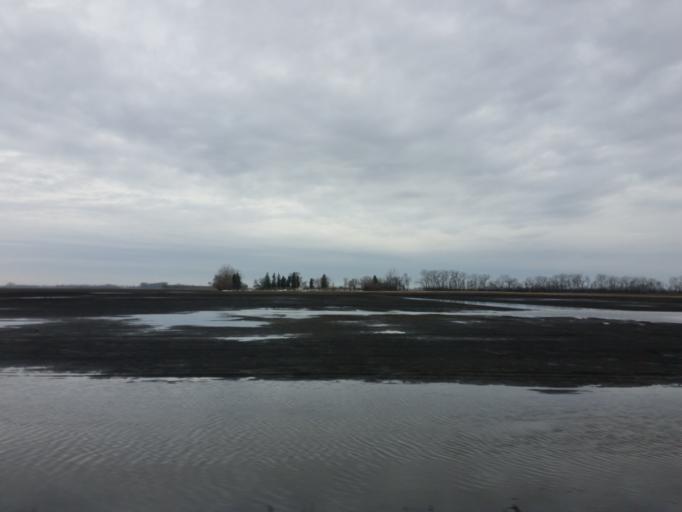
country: US
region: North Dakota
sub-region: Walsh County
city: Grafton
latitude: 48.3968
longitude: -97.4703
